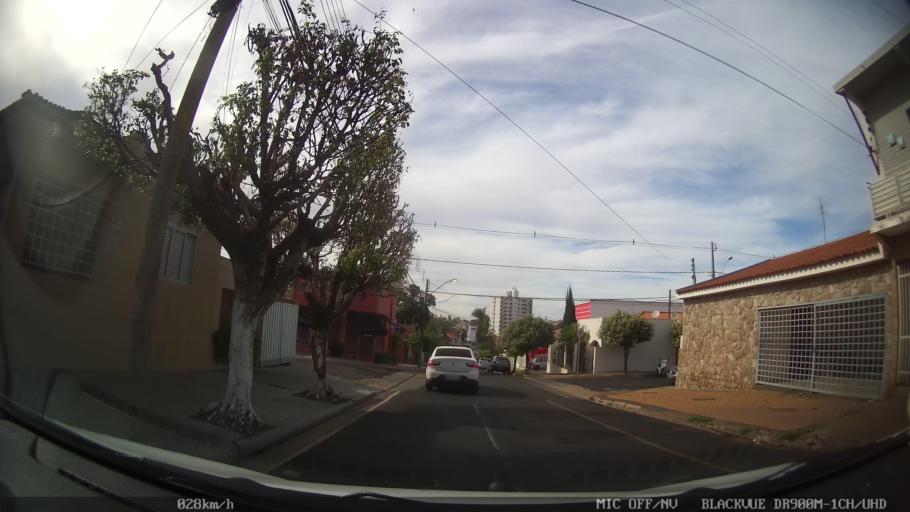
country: BR
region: Sao Paulo
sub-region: Catanduva
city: Catanduva
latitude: -21.1407
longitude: -48.9702
